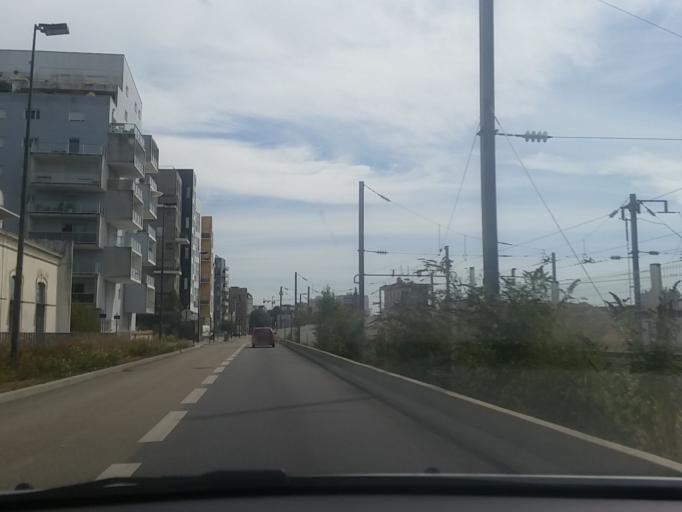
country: FR
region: Pays de la Loire
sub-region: Departement de la Loire-Atlantique
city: Nantes
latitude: 47.2041
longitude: -1.5593
